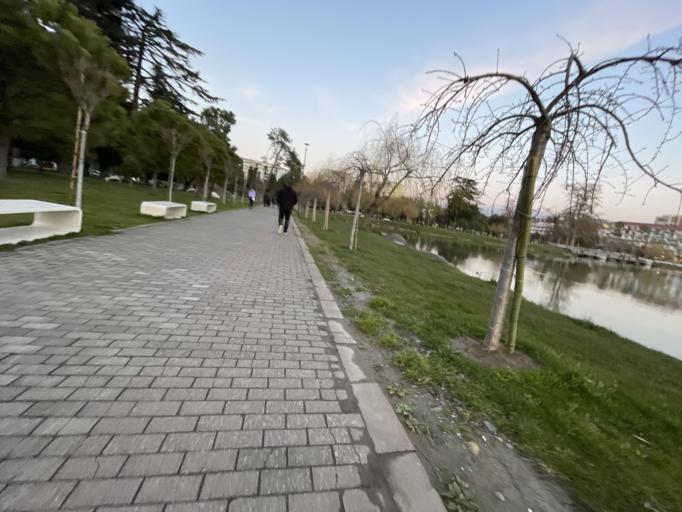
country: GE
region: Ajaria
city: Batumi
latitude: 41.6486
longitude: 41.6271
